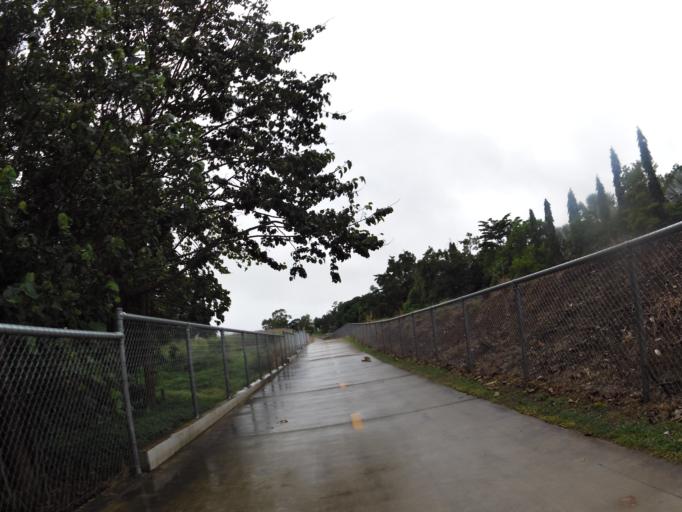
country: AU
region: Queensland
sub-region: Cairns
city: Redlynch
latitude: -16.8837
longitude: 145.7046
